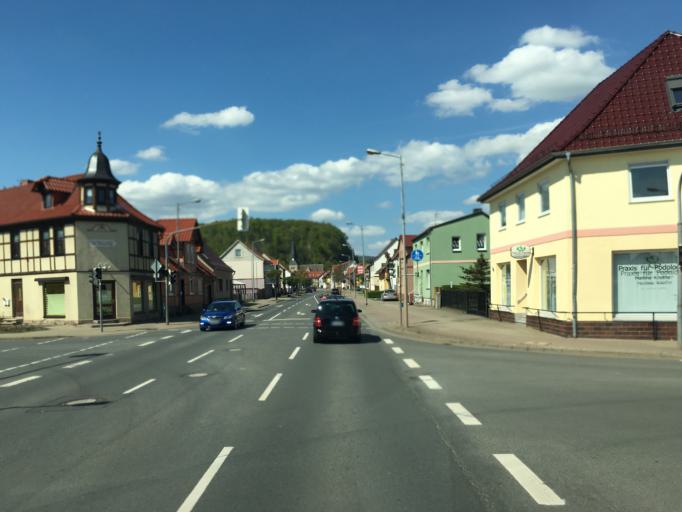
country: DE
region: Thuringia
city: Niedersachswerfen
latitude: 51.5504
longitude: 10.7677
